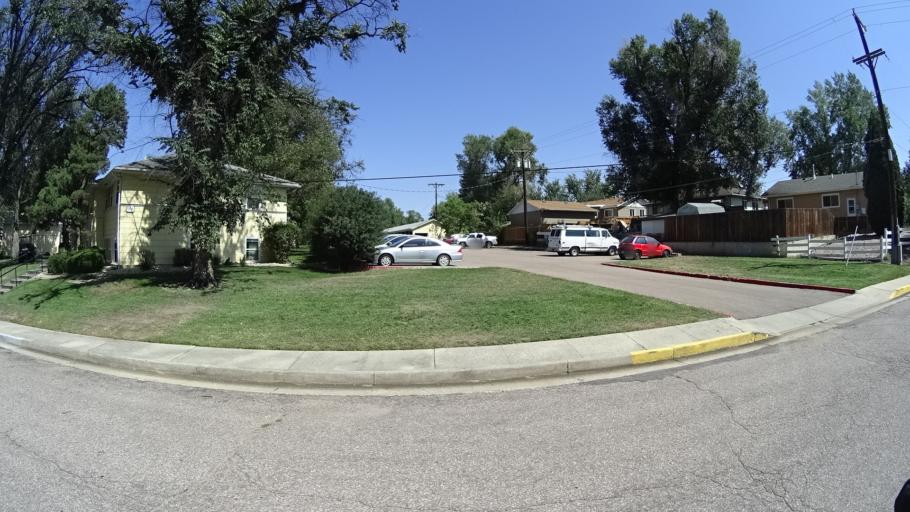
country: US
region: Colorado
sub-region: El Paso County
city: Colorado Springs
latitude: 38.8510
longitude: -104.8005
